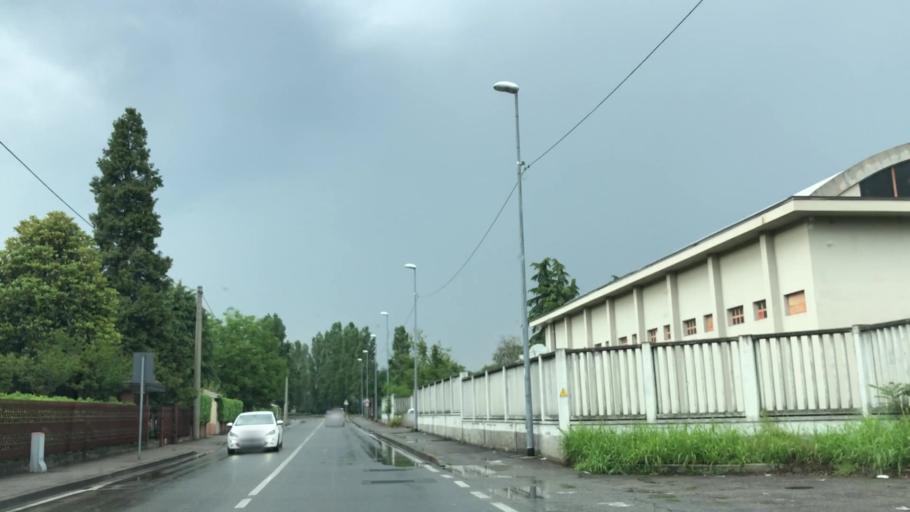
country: IT
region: Lombardy
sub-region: Citta metropolitana di Milano
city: Paderno Dugnano
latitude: 45.5719
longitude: 9.1709
